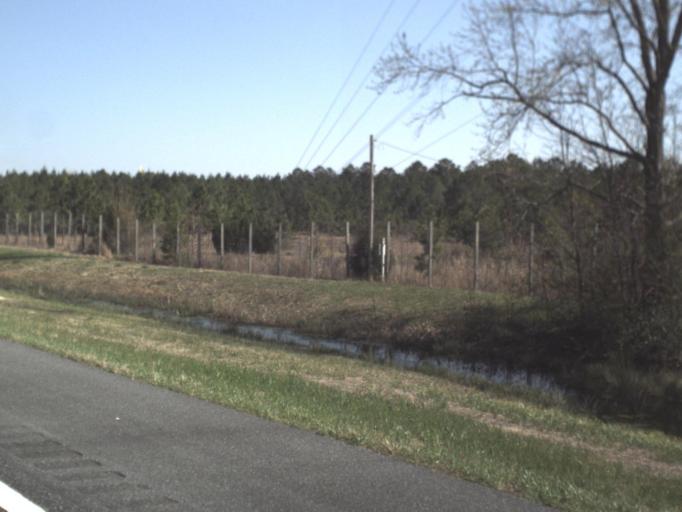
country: US
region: Florida
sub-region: Washington County
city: Chipley
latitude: 30.7514
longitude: -85.3909
